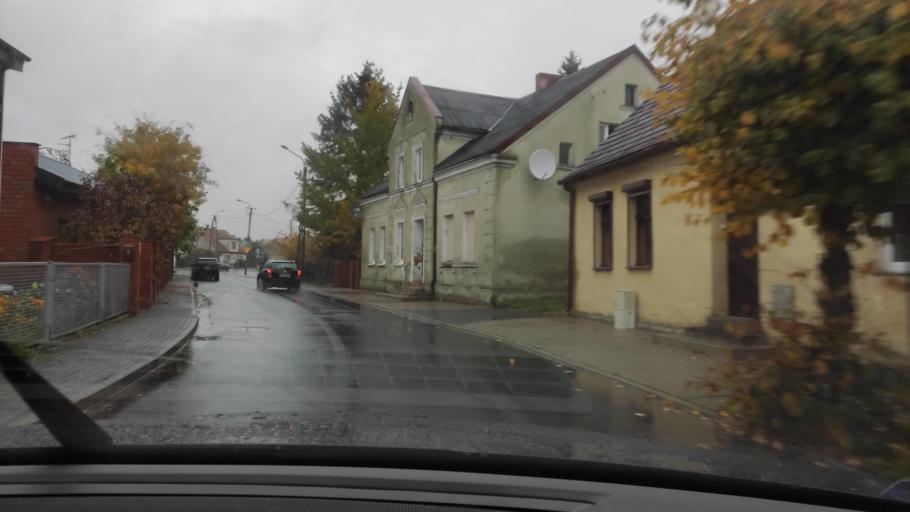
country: PL
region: Greater Poland Voivodeship
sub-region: Powiat poznanski
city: Kornik
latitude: 52.2287
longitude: 17.0944
